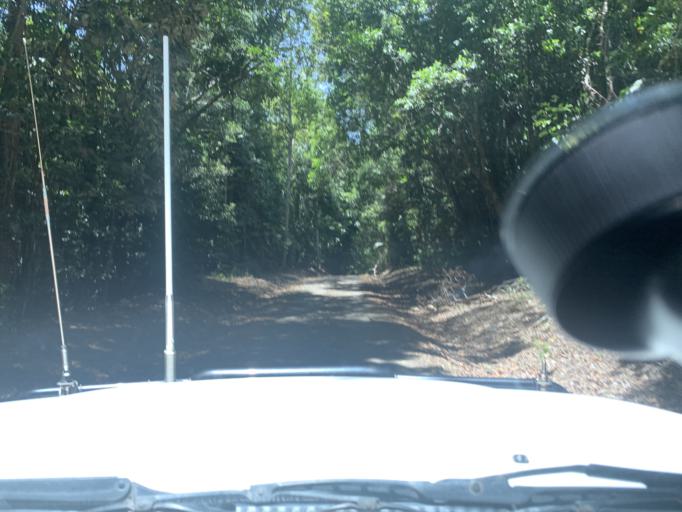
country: AU
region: Queensland
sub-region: Cairns
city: Redlynch
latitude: -16.9656
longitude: 145.6470
